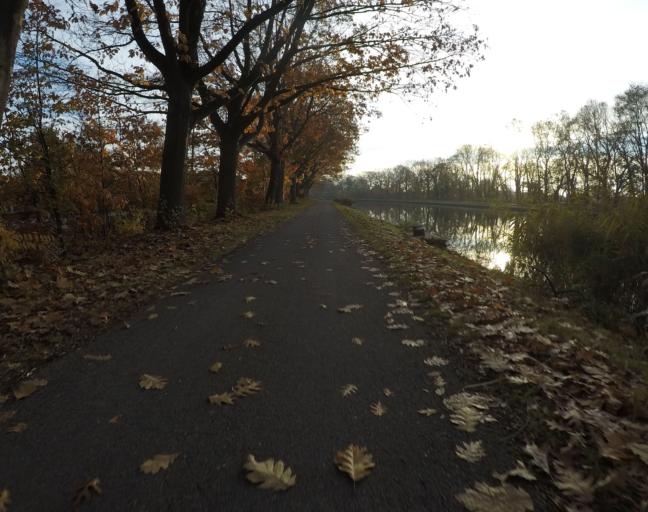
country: BE
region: Flanders
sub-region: Provincie Antwerpen
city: Herentals
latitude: 51.1692
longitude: 4.8344
